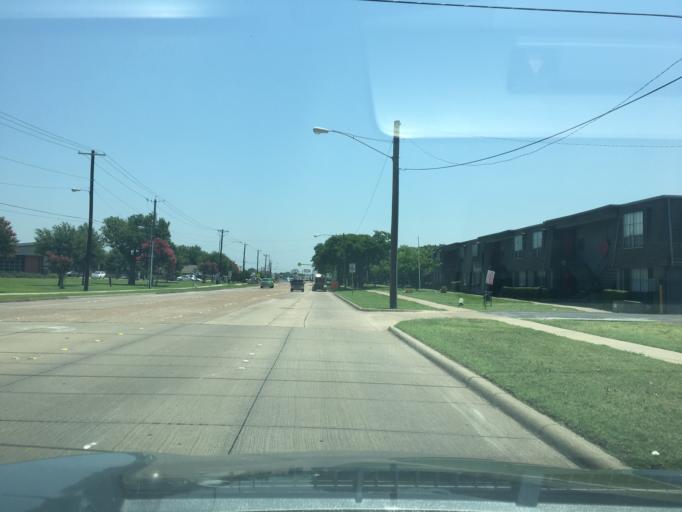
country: US
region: Texas
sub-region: Dallas County
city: Richardson
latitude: 32.9167
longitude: -96.6919
